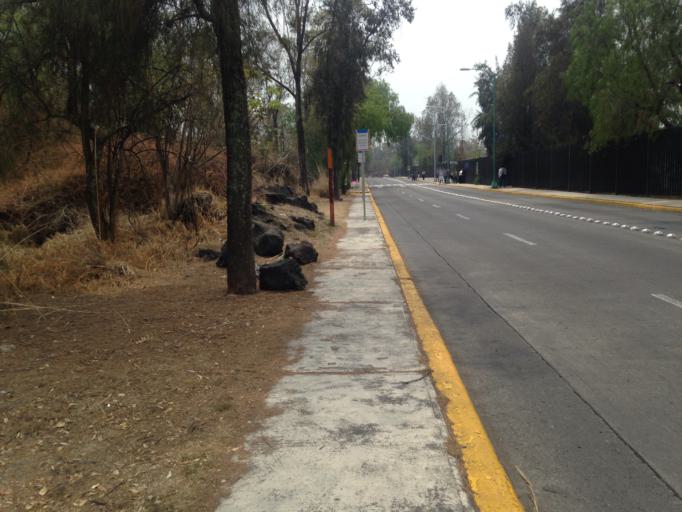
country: MX
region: Mexico City
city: Magdalena Contreras
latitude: 19.3240
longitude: -99.1838
